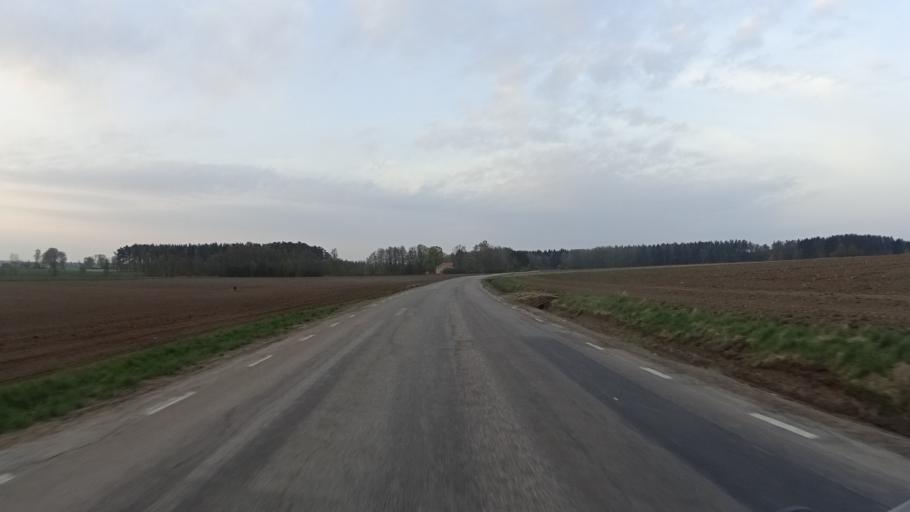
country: SE
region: Vaestra Goetaland
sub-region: Gotene Kommun
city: Kallby
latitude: 58.4919
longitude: 13.3156
